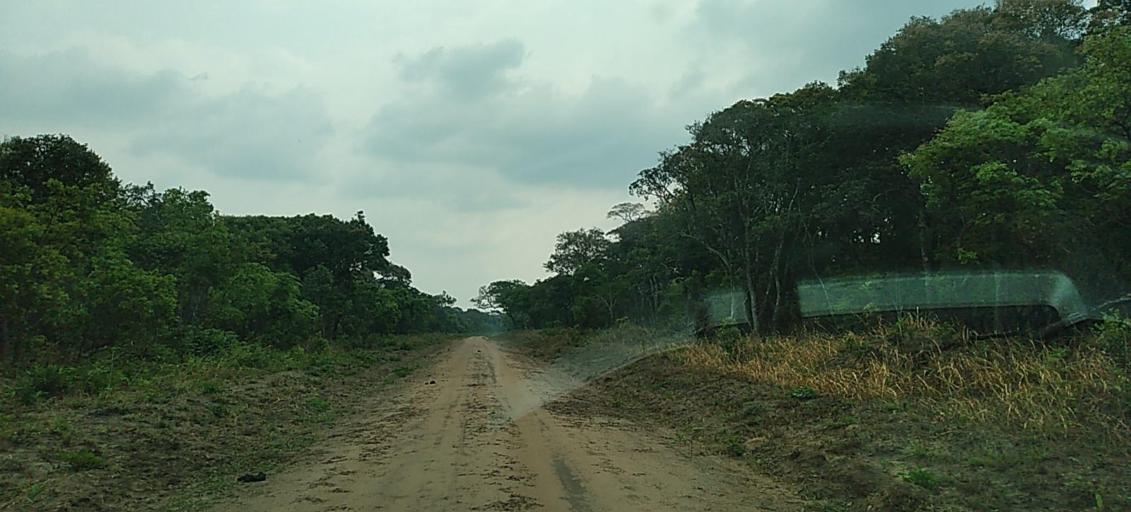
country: ZM
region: North-Western
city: Mwinilunga
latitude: -11.4127
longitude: 24.6147
